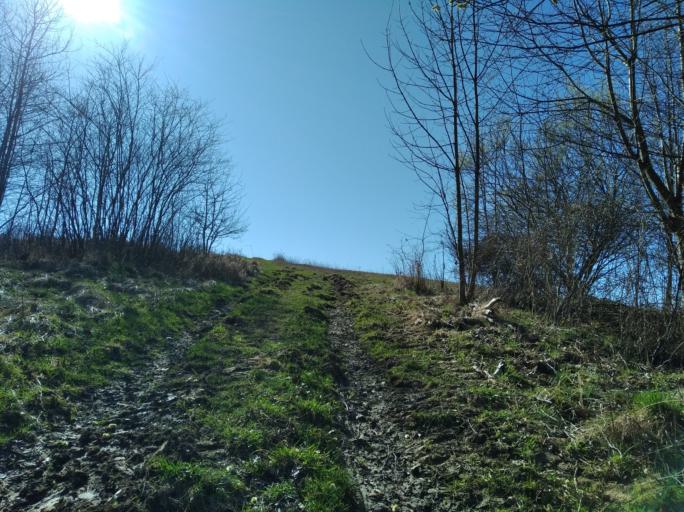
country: PL
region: Subcarpathian Voivodeship
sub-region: Powiat strzyzowski
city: Strzyzow
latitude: 49.8291
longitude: 21.8356
